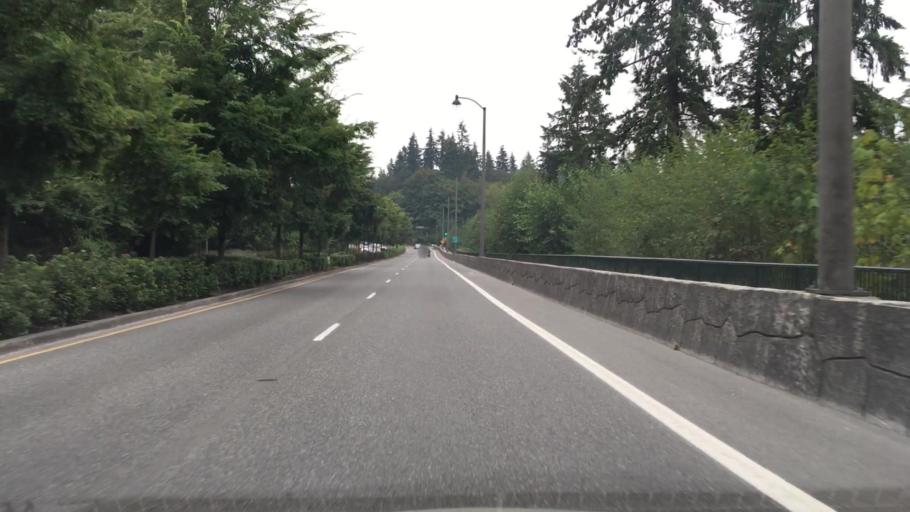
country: US
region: Washington
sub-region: King County
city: Newcastle
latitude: 47.5262
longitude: -122.1639
